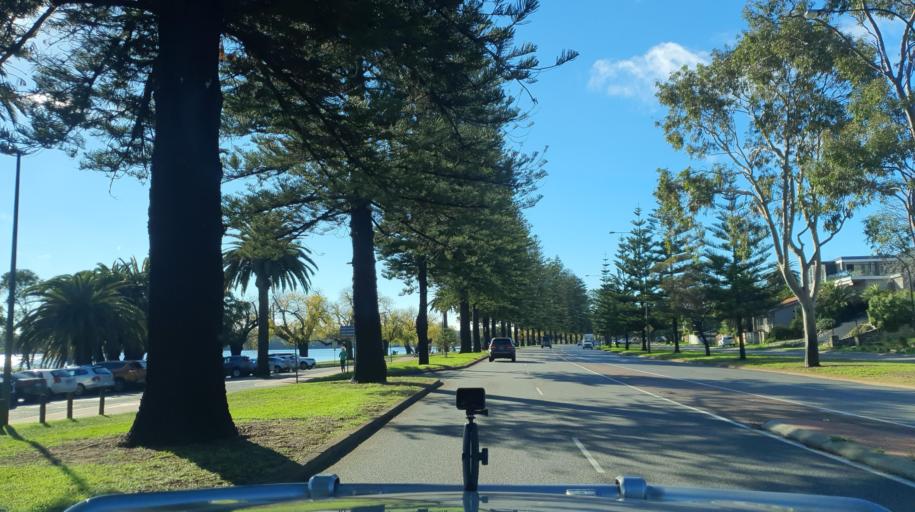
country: AU
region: Western Australia
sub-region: Cambridge
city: West Leederville
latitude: -31.9336
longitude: 115.8250
